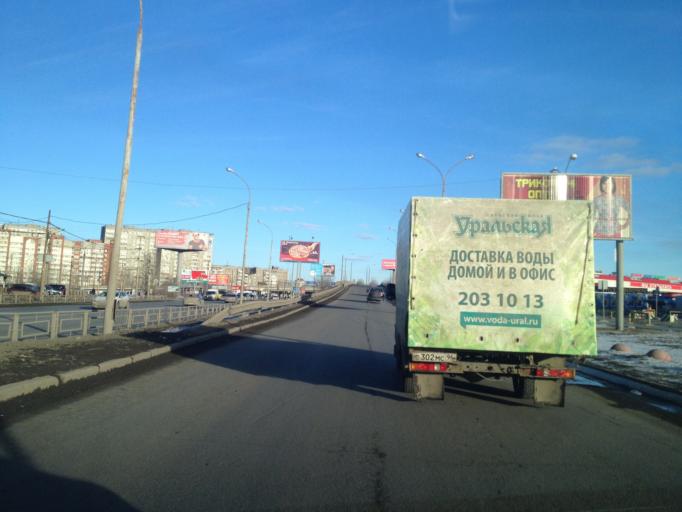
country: RU
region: Sverdlovsk
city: Yekaterinburg
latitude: 56.8616
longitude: 60.5443
